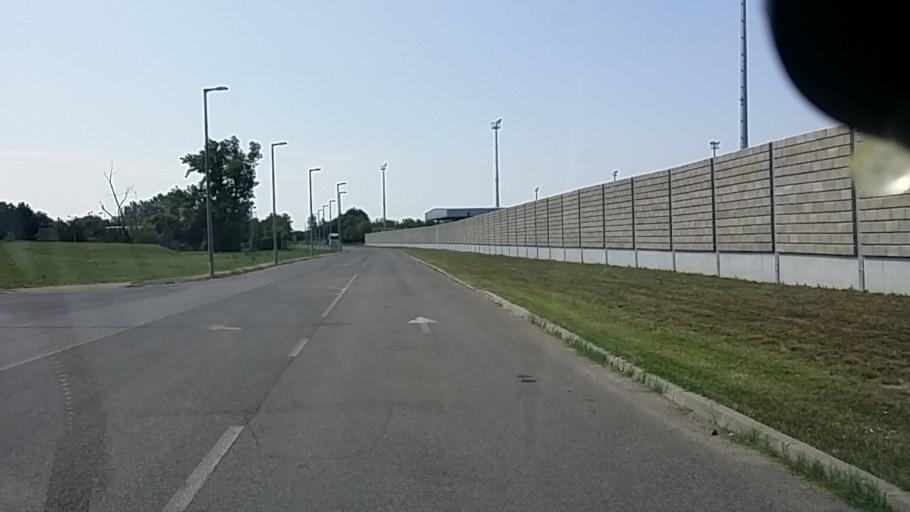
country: HU
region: Budapest
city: Budapest XXII. keruelet
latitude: 47.4165
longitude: 19.0518
